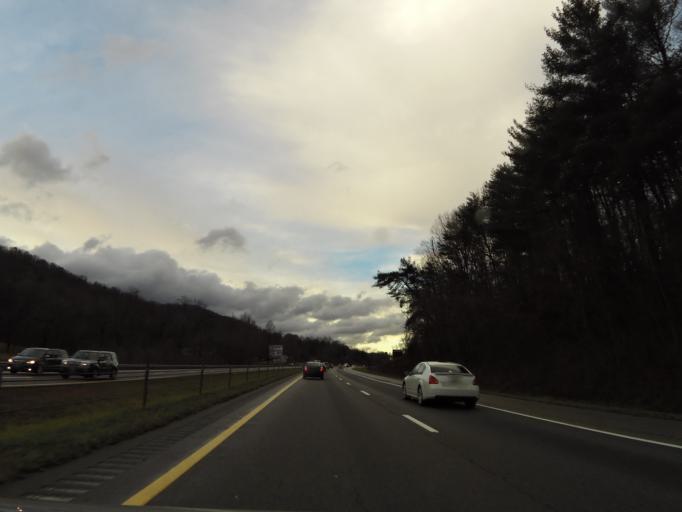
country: US
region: Tennessee
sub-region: Anderson County
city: Rocky Top
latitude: 36.2475
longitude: -84.1800
